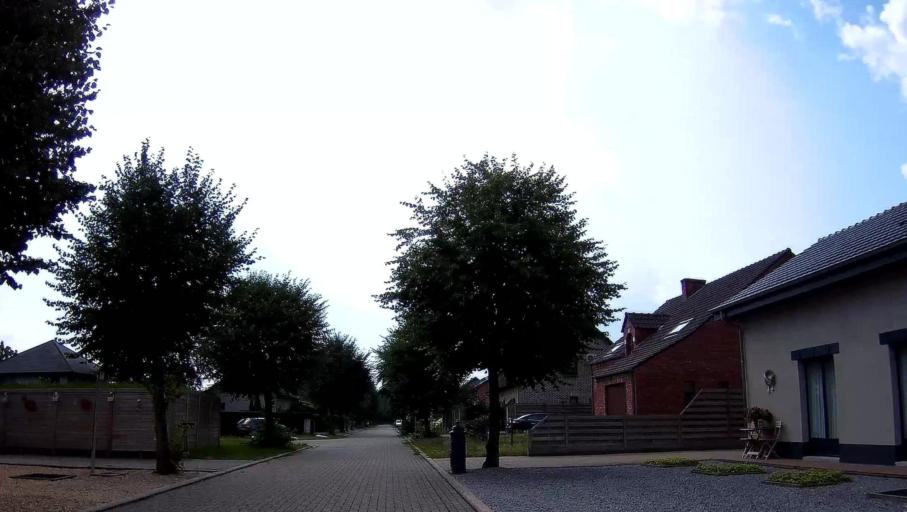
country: BE
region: Flanders
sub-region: Provincie Limburg
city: Lommel
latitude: 51.2210
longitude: 5.2600
